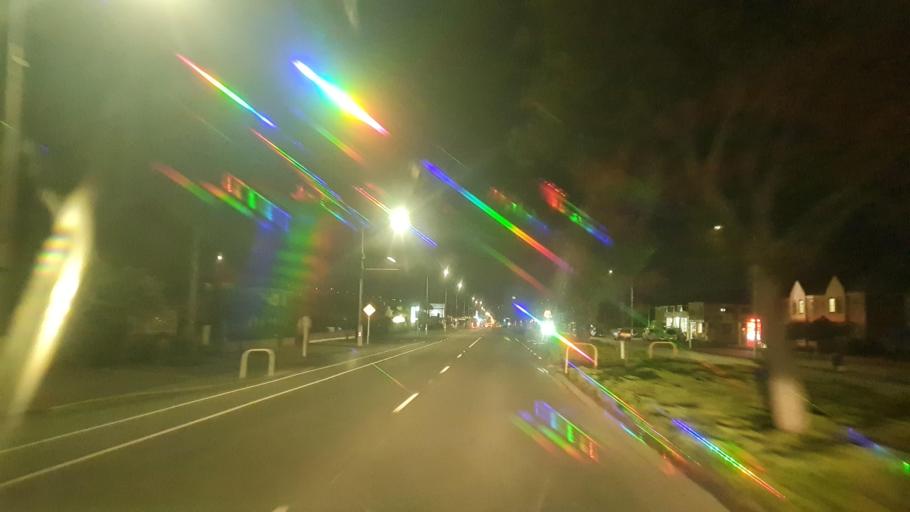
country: NZ
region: Otago
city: Oamaru
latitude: -45.0907
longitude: 170.9745
